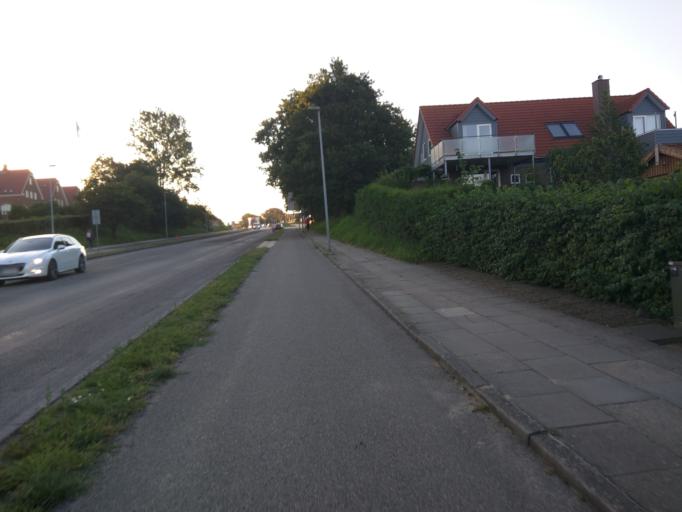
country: DK
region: Central Jutland
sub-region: Viborg Kommune
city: Viborg
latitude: 56.4491
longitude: 9.4271
